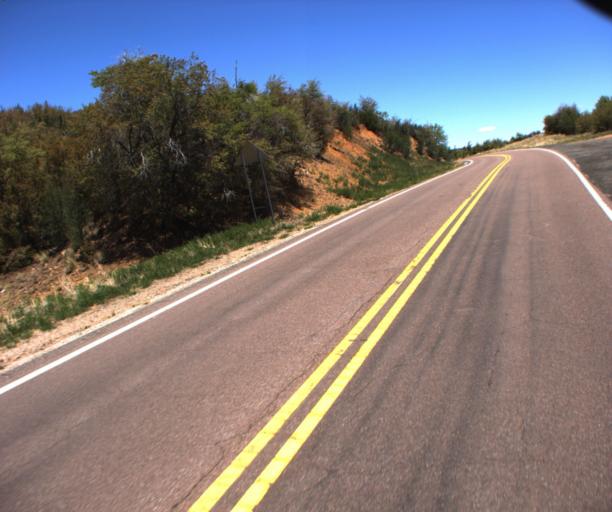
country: US
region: Arizona
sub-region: Yavapai County
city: Prescott
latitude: 34.4894
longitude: -112.5011
